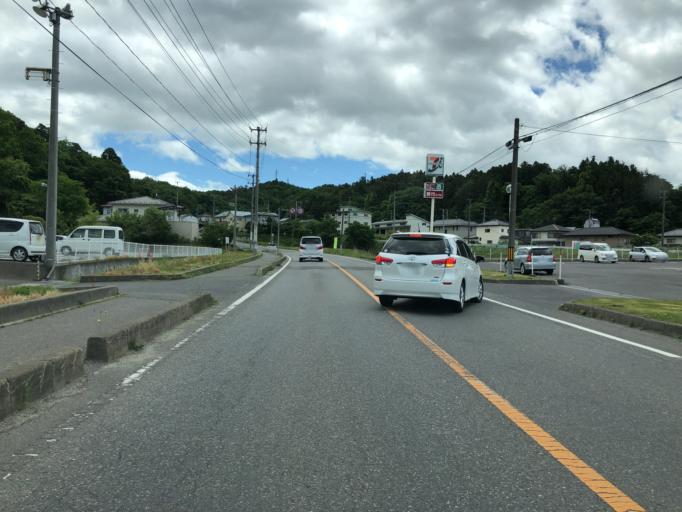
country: JP
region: Fukushima
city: Motomiya
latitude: 37.5133
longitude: 140.4114
